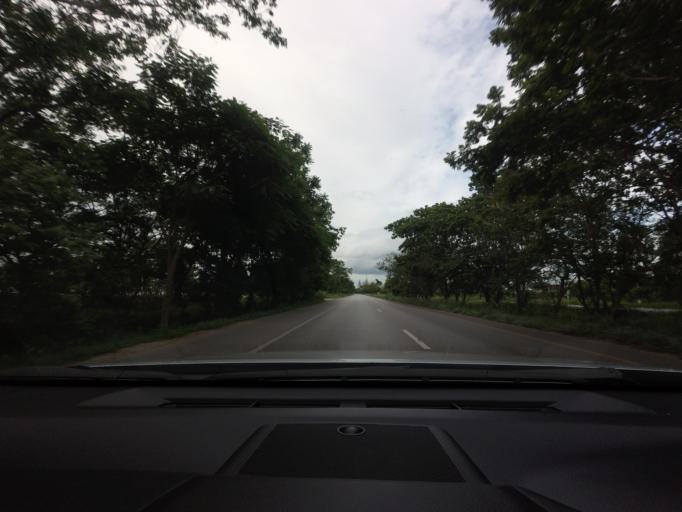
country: TH
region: Phetchaburi
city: Cha-am
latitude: 12.7244
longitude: 99.9239
